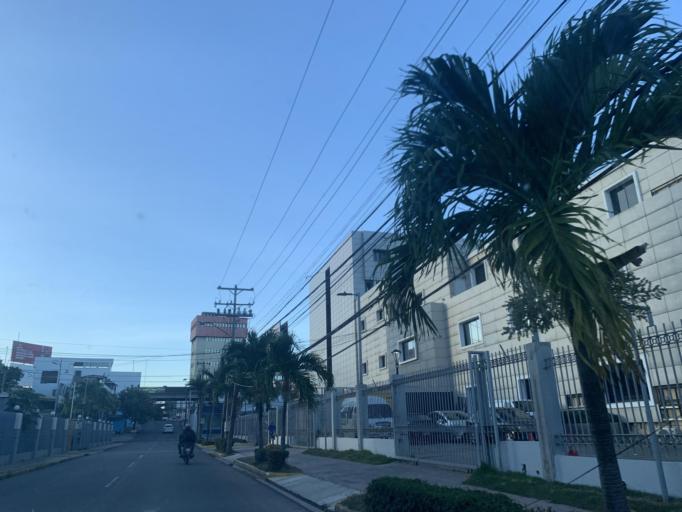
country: DO
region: Nacional
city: Ciudad Nueva
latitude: 18.4746
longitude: -69.9057
